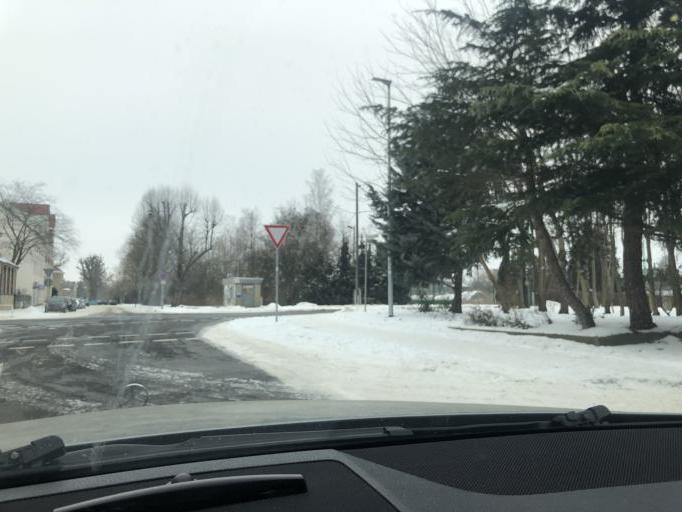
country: DE
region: Brandenburg
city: Guben
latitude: 51.9477
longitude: 14.7095
